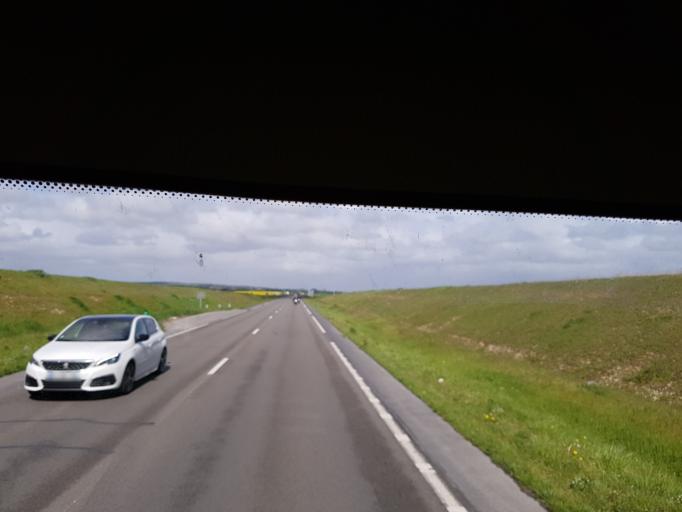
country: FR
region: Nord-Pas-de-Calais
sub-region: Departement du Nord
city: Proville
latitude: 50.1446
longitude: 3.2079
